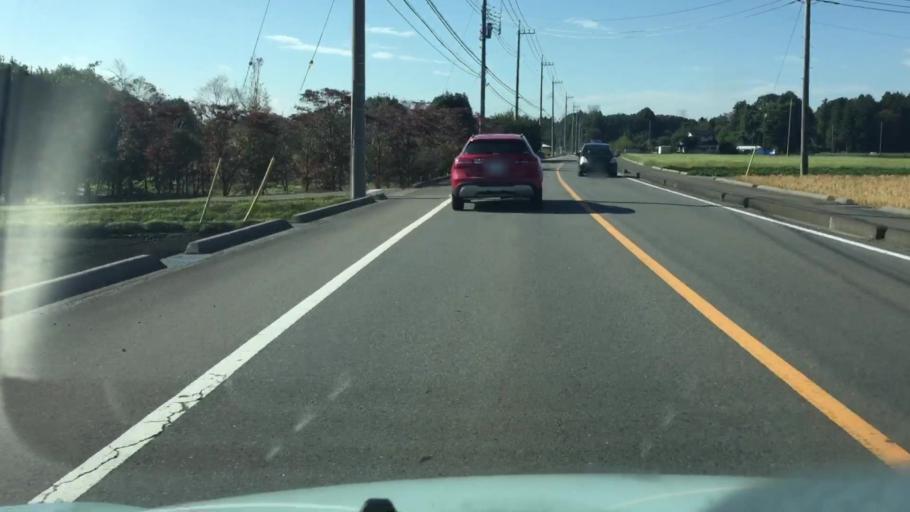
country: JP
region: Tochigi
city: Utsunomiya-shi
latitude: 36.5806
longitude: 139.9815
